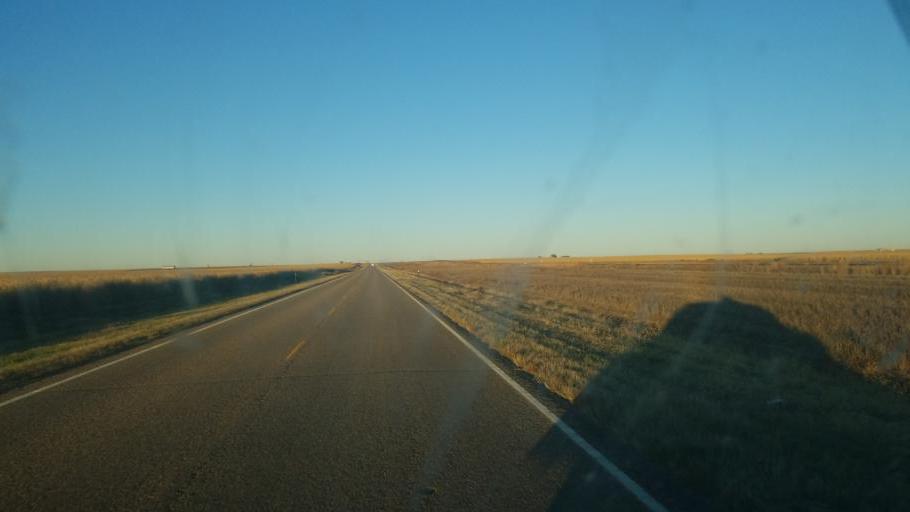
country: US
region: Colorado
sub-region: Cheyenne County
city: Cheyenne Wells
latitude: 38.8505
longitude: -102.0946
